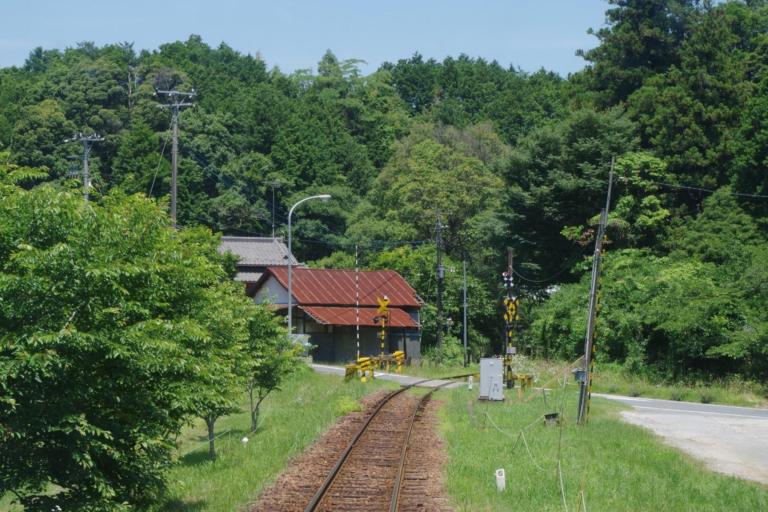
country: JP
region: Chiba
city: Mobara
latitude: 35.3211
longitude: 140.1420
